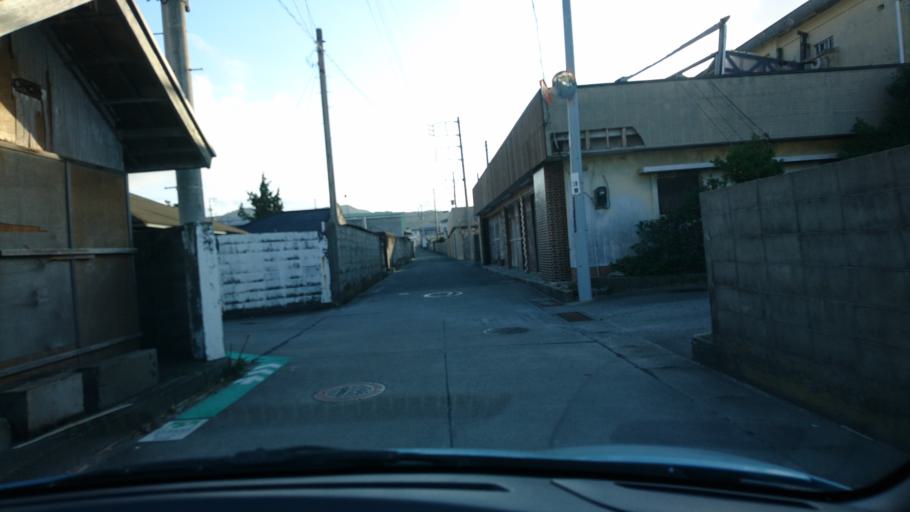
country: JP
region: Shizuoka
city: Shimoda
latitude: 34.3791
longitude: 139.2548
